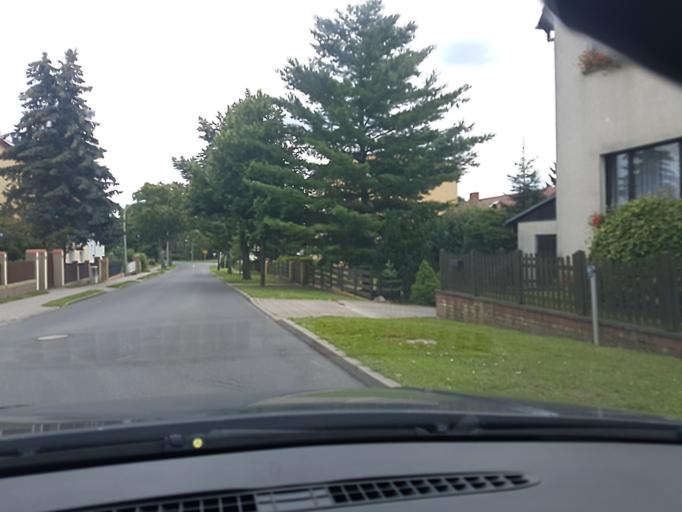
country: DE
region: Brandenburg
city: Velten
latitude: 52.6774
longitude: 13.1621
